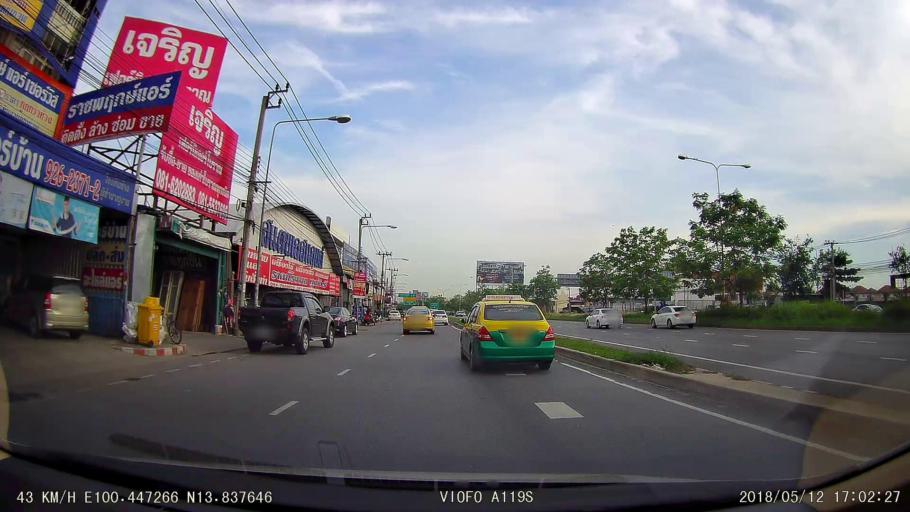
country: TH
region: Nonthaburi
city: Bang Kruai
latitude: 13.8376
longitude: 100.4473
